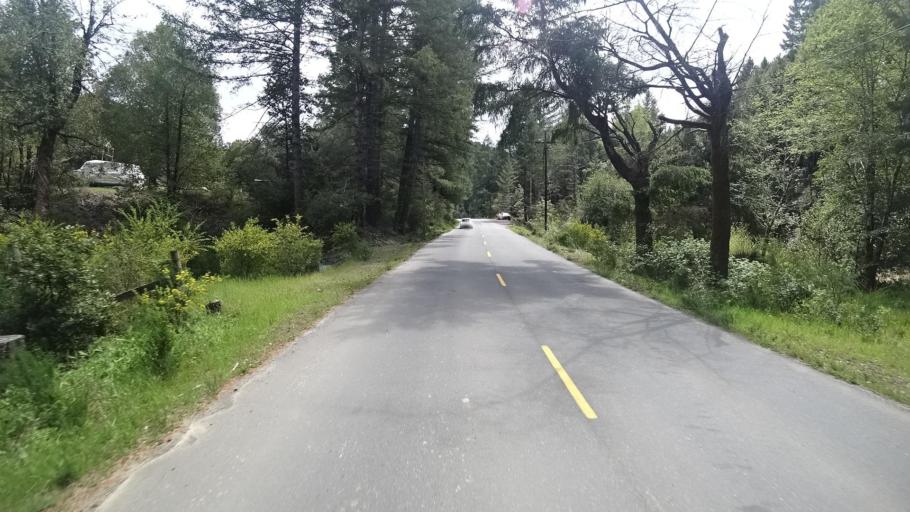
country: US
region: California
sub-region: Humboldt County
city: Redway
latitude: 40.0915
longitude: -123.9372
